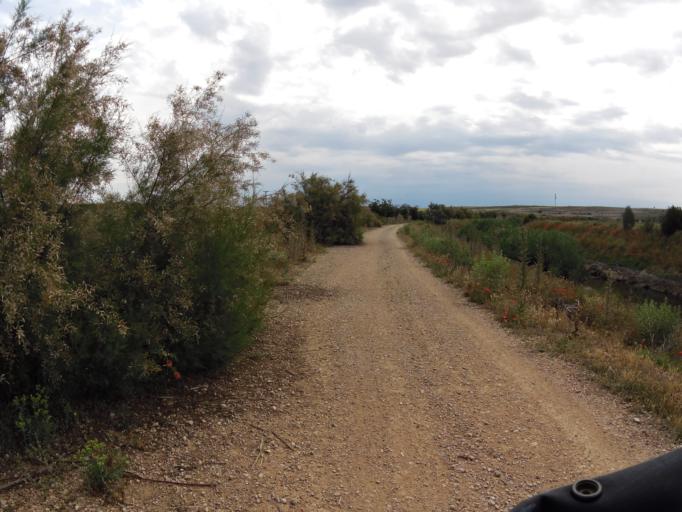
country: ES
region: Castille-La Mancha
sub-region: Provincia de Albacete
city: Valdeganga
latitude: 39.0604
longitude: -1.7553
